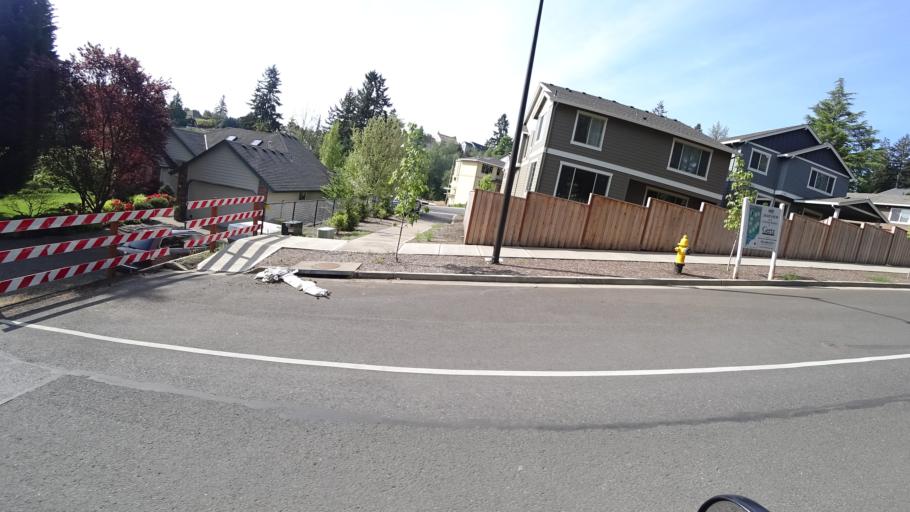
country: US
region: Oregon
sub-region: Washington County
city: Aloha
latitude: 45.4531
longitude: -122.8424
